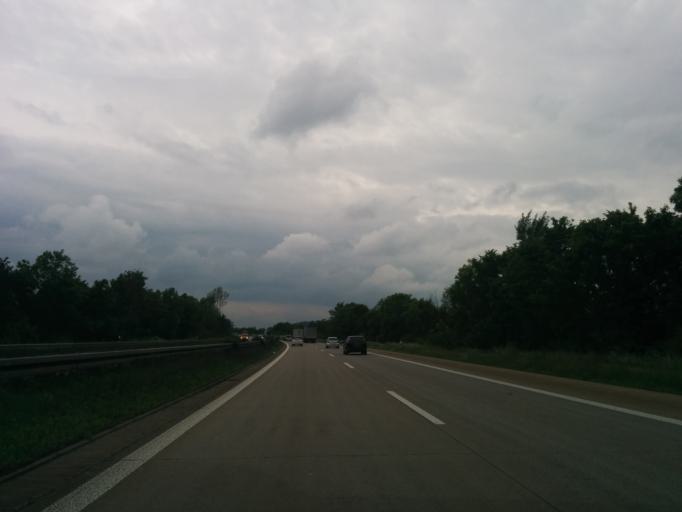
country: DE
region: Bavaria
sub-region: Regierungsbezirk Mittelfranken
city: Schopfloch
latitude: 49.1513
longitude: 10.2659
